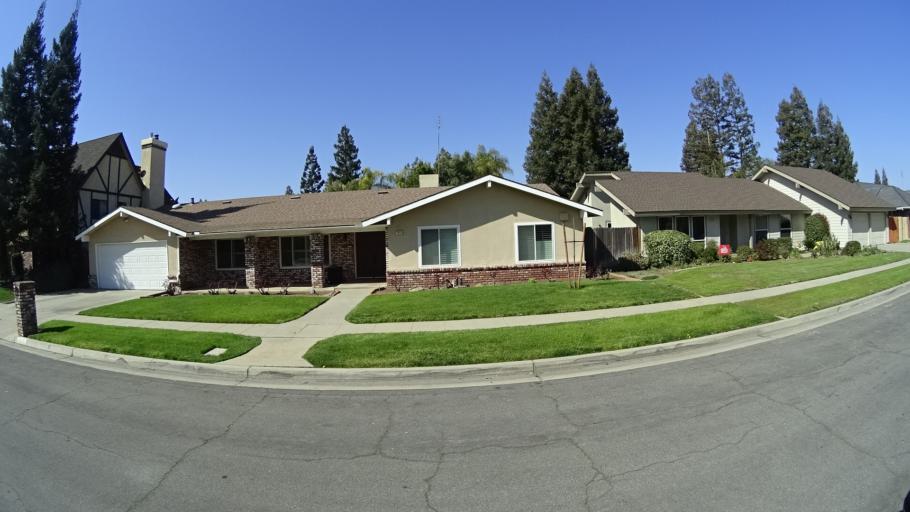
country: US
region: California
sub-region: Fresno County
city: Fresno
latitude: 36.8412
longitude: -119.8216
